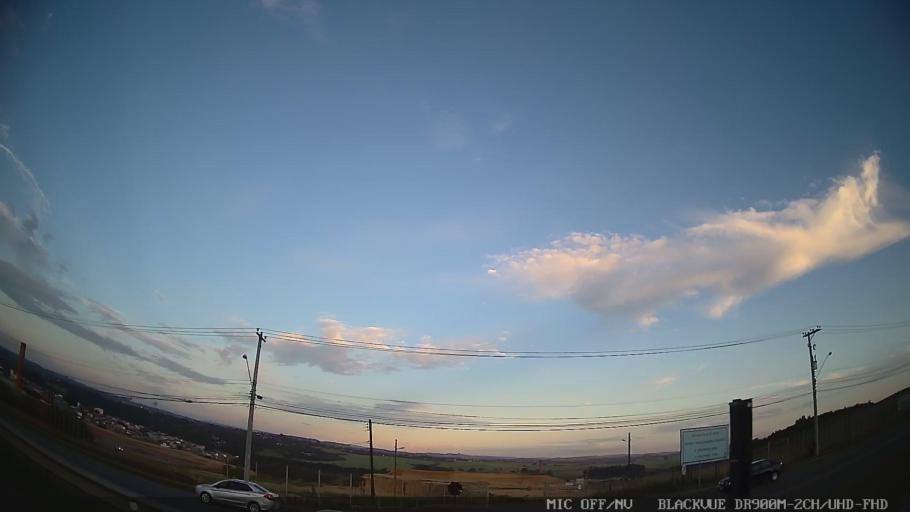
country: BR
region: Sao Paulo
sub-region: Indaiatuba
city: Indaiatuba
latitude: -23.1102
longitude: -47.2083
